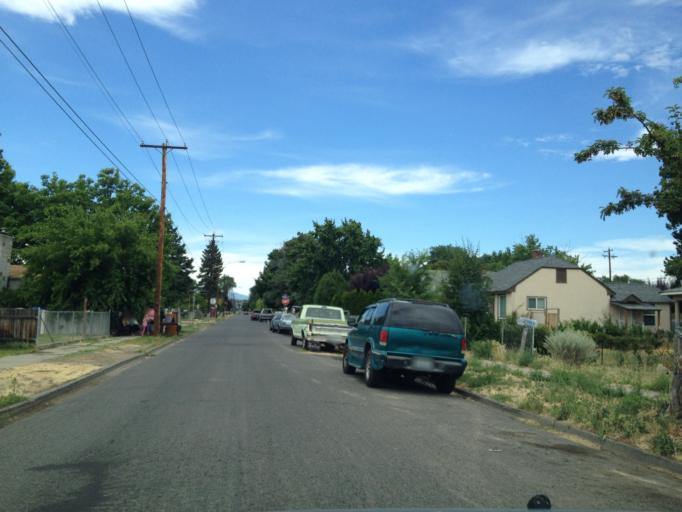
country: US
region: Washington
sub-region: Yakima County
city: Yakima
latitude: 46.6071
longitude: -120.5225
